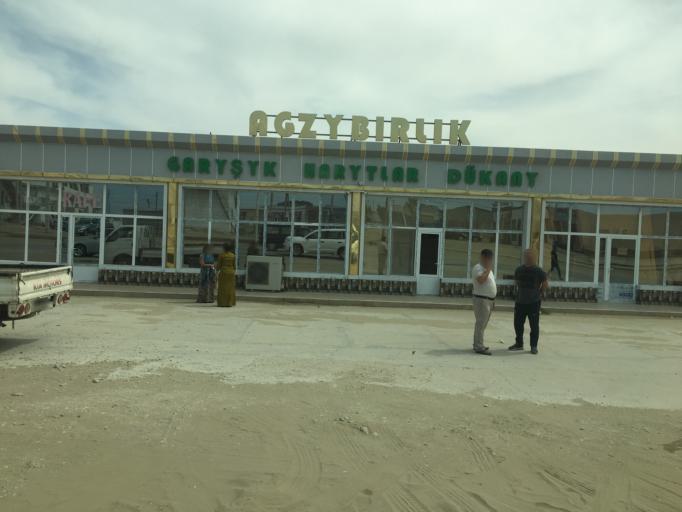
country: TM
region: Balkan
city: Turkmenbasy
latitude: 39.4087
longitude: 53.1303
